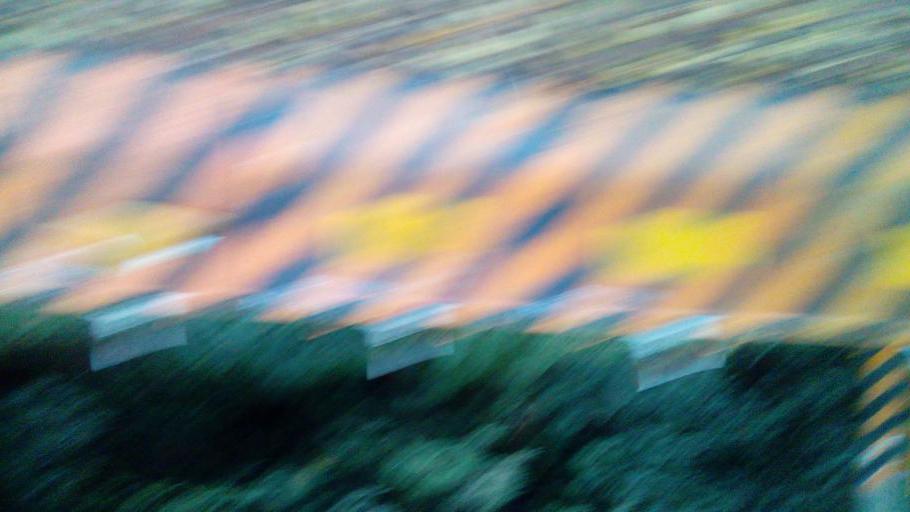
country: TW
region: Taiwan
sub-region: Hualien
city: Hualian
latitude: 24.3382
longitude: 121.3133
